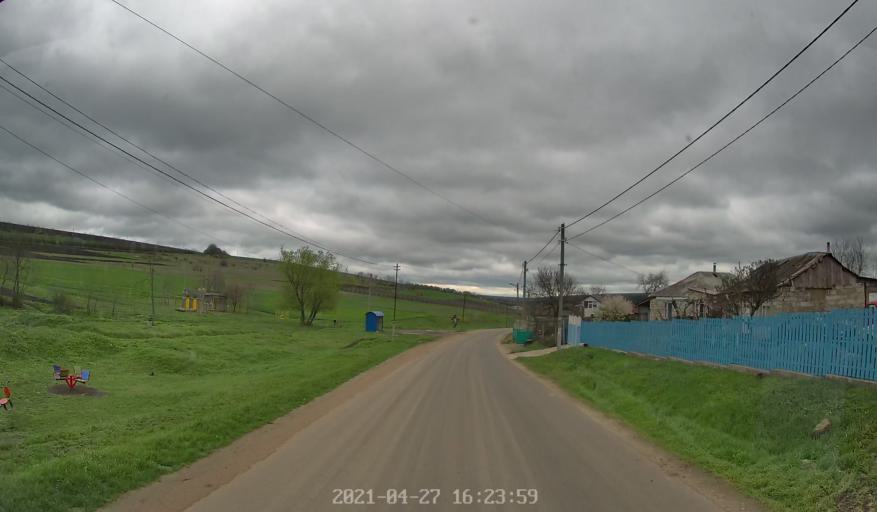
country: MD
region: Chisinau
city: Singera
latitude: 46.9951
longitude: 29.0201
